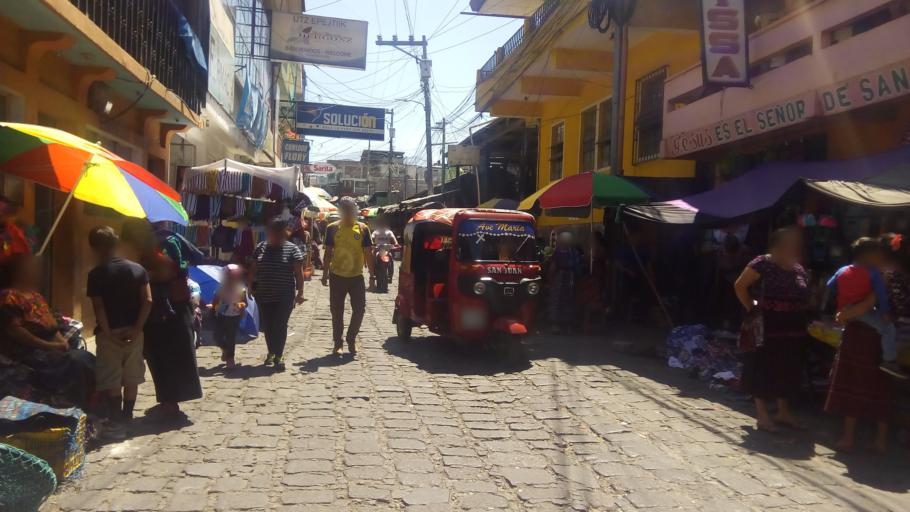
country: GT
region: Solola
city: San Pedro La Laguna
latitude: 14.6920
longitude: -91.2728
